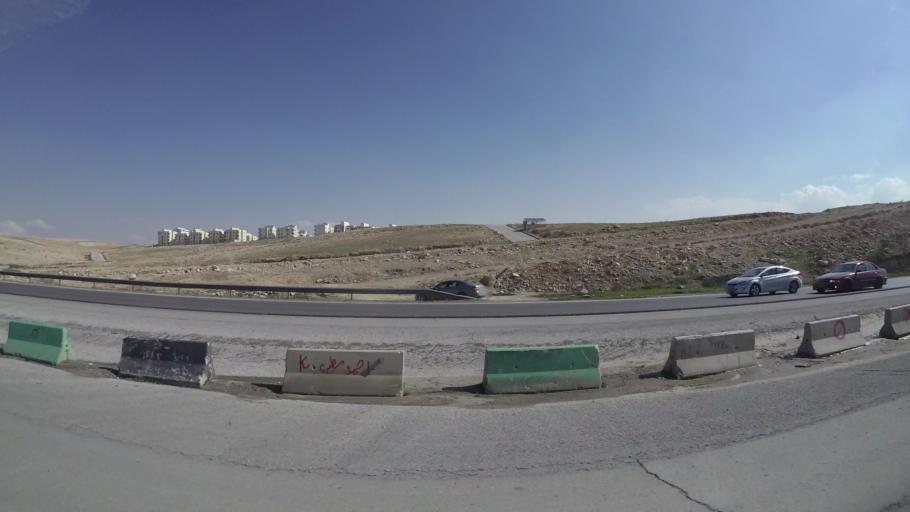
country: JO
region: Zarqa
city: Zarqa
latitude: 32.0406
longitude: 36.1066
